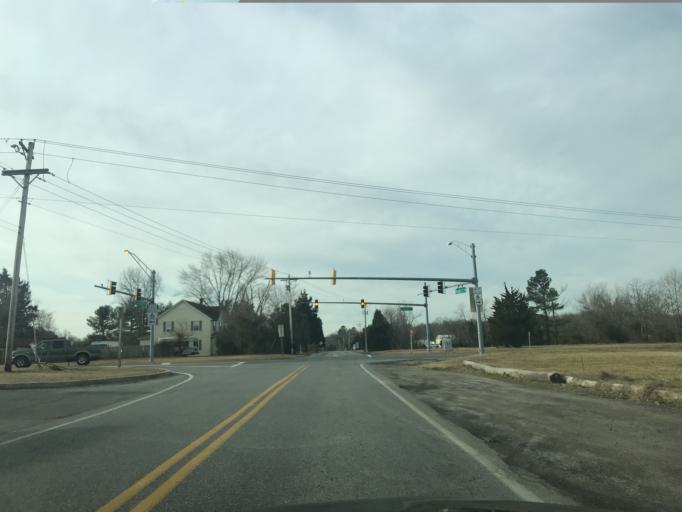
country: US
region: Maryland
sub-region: Charles County
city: La Plata
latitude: 38.4823
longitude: -76.8923
